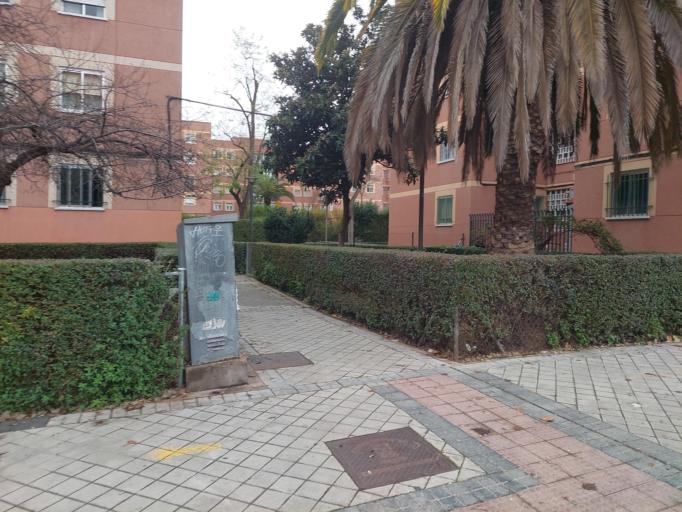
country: ES
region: Madrid
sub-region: Provincia de Madrid
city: Leganes
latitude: 40.3281
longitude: -3.7699
